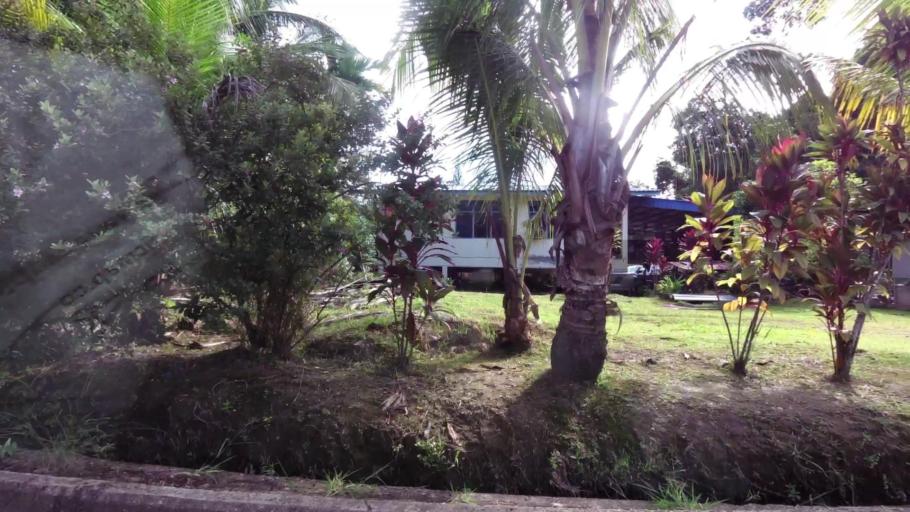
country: BN
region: Brunei and Muara
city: Bandar Seri Begawan
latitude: 4.9001
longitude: 114.9718
